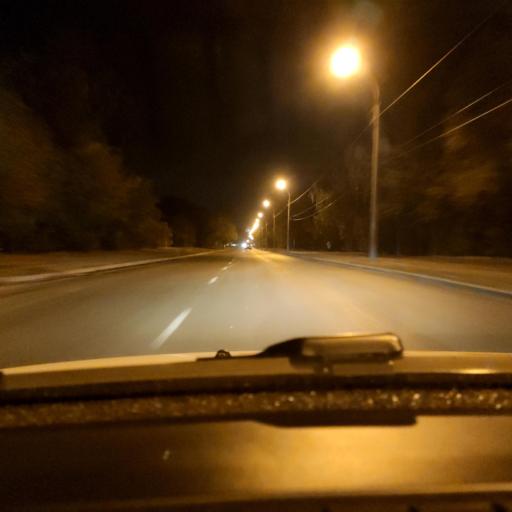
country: RU
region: Voronezj
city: Voronezh
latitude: 51.6420
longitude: 39.2109
